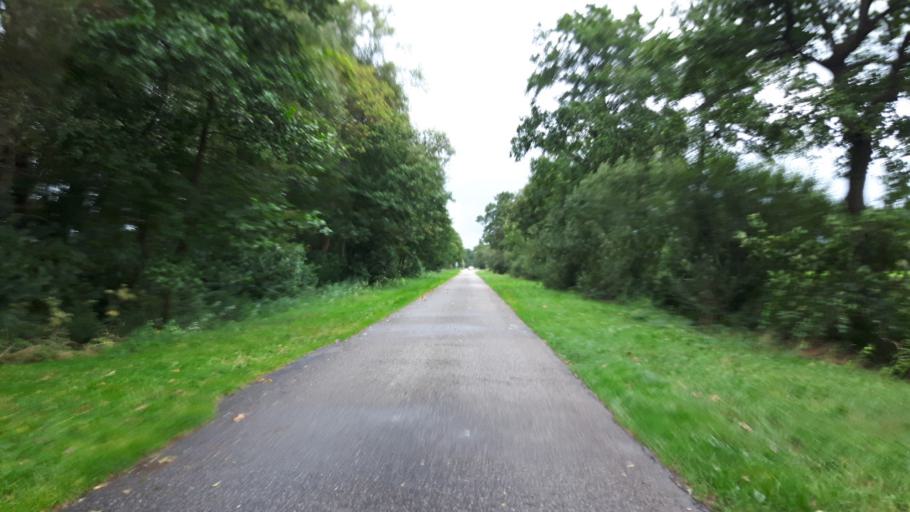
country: NL
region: Friesland
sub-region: Gemeente Dantumadiel
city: Broeksterwald
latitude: 53.2687
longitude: 5.9836
